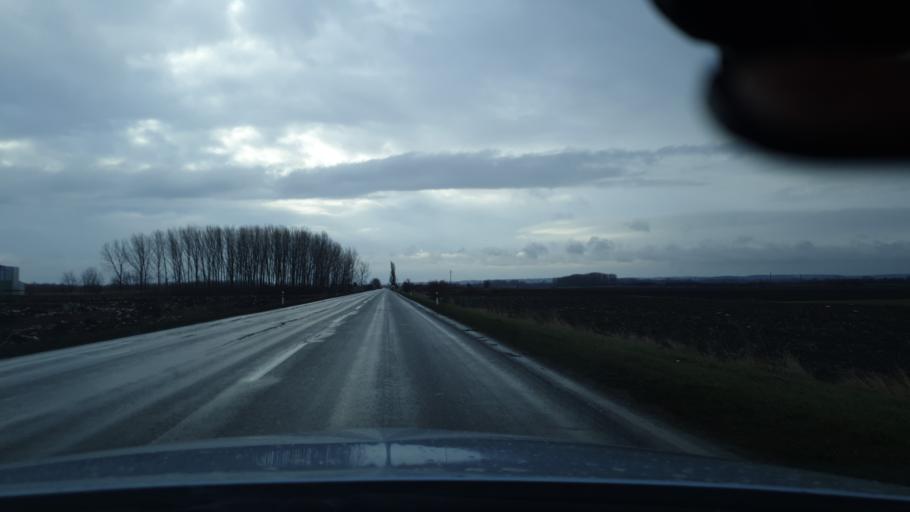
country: RS
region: Autonomna Pokrajina Vojvodina
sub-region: Juznobanatski Okrug
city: Kovin
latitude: 44.7289
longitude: 20.9649
